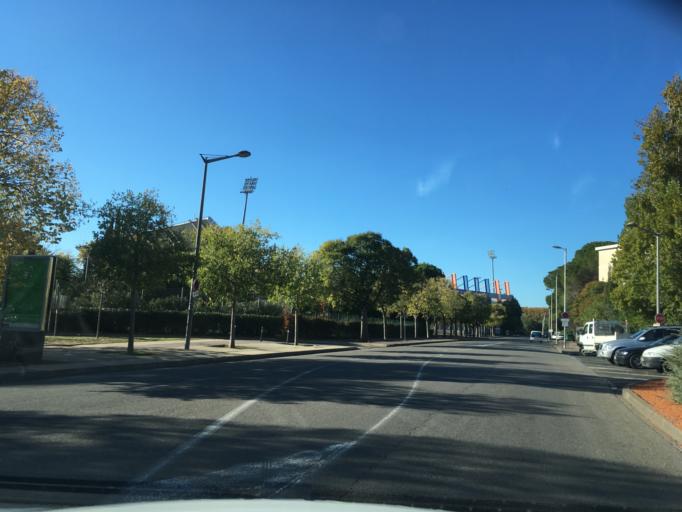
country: FR
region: Languedoc-Roussillon
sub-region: Departement de l'Herault
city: Juvignac
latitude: 43.6214
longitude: 3.8153
